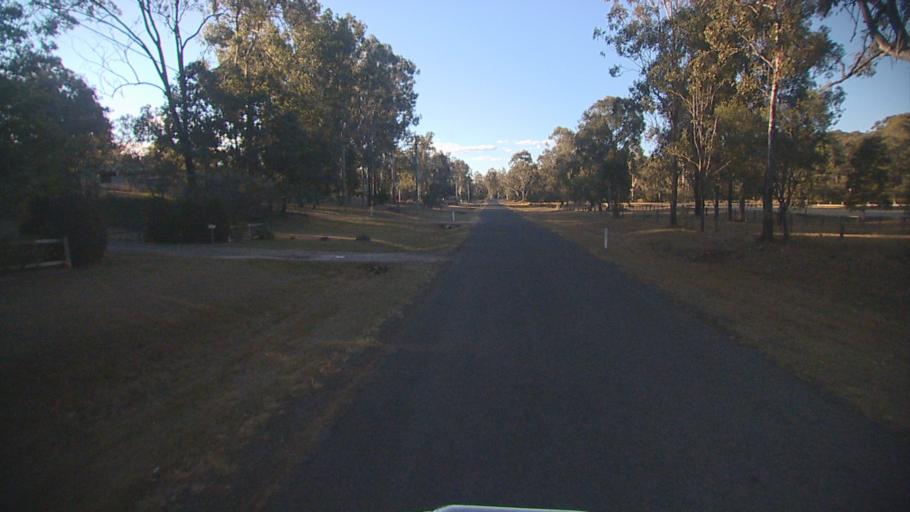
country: AU
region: Queensland
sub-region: Logan
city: Cedar Vale
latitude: -27.8660
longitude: 152.9768
